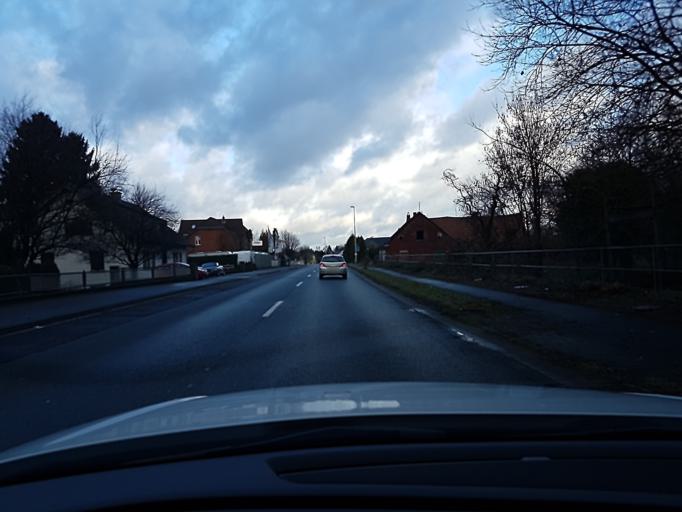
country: DE
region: North Rhine-Westphalia
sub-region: Regierungsbezirk Dusseldorf
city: Muelheim (Ruhr)
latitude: 51.3797
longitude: 6.8631
